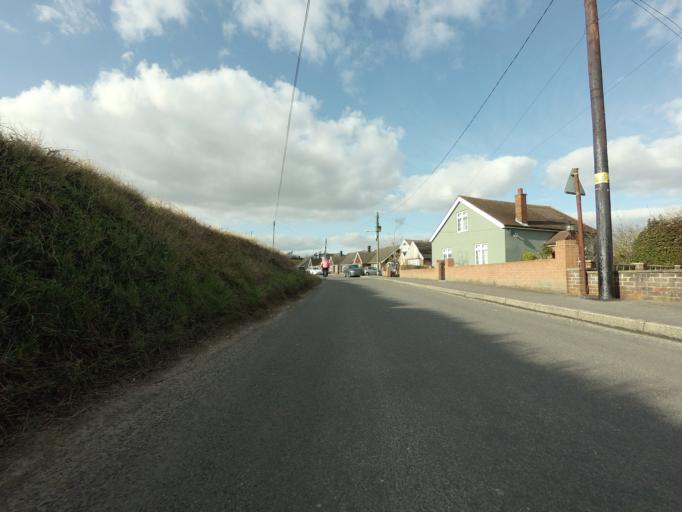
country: GB
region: England
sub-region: Kent
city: Dartford
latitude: 51.4205
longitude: 0.2200
